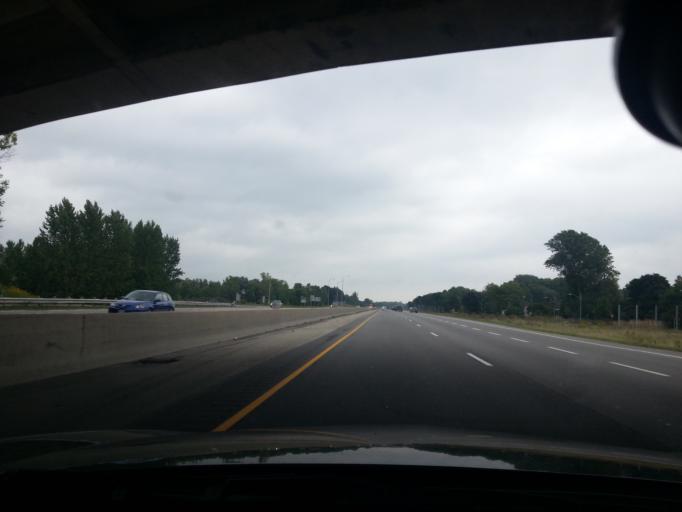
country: CA
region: Ontario
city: Brockville
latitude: 44.6112
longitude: -75.6851
